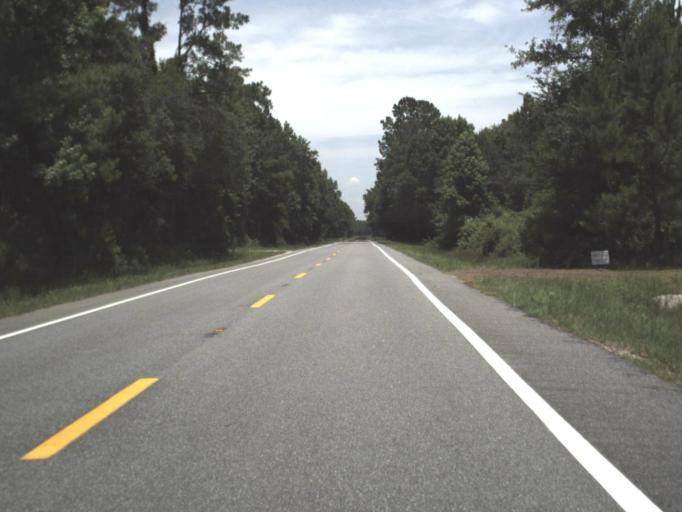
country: US
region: Florida
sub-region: Lafayette County
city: Mayo
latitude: 29.9038
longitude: -83.2942
